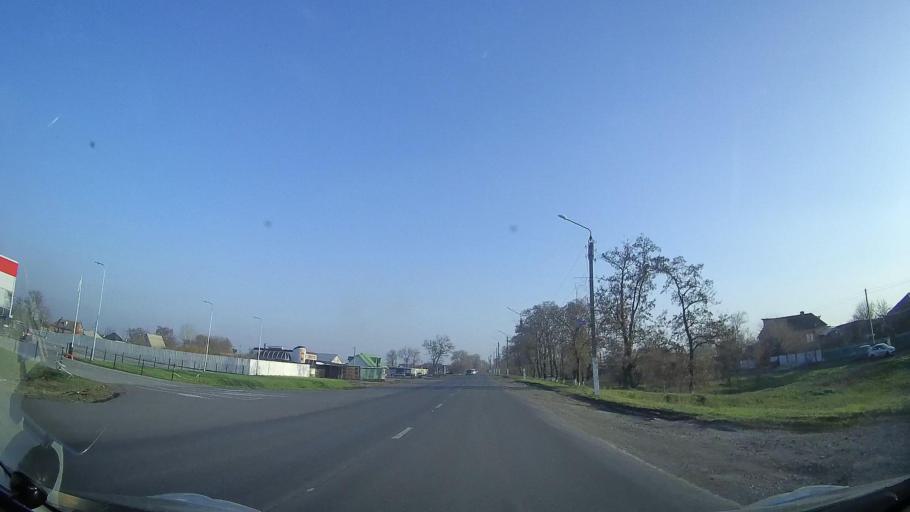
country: RU
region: Rostov
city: Ol'ginskaya
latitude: 47.1996
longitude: 39.9348
